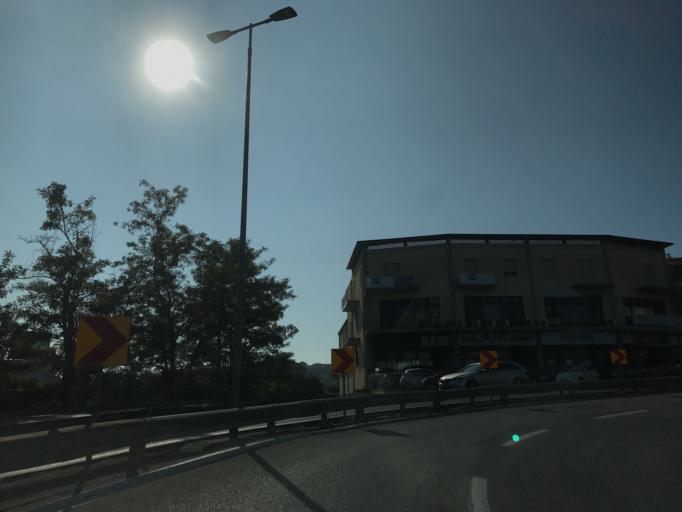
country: SM
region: Serravalle
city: Serravalle
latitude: 43.9709
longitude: 12.4830
